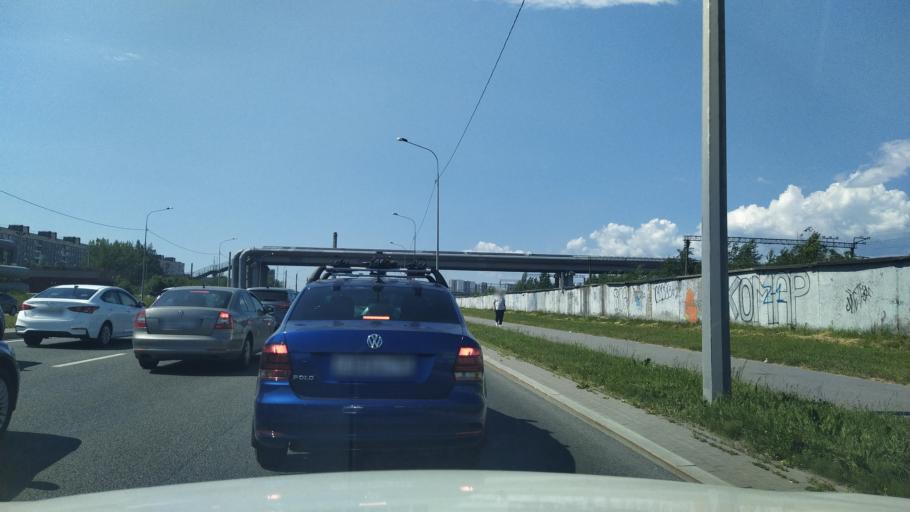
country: RU
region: Leningrad
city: Parnas
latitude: 60.0588
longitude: 30.3507
